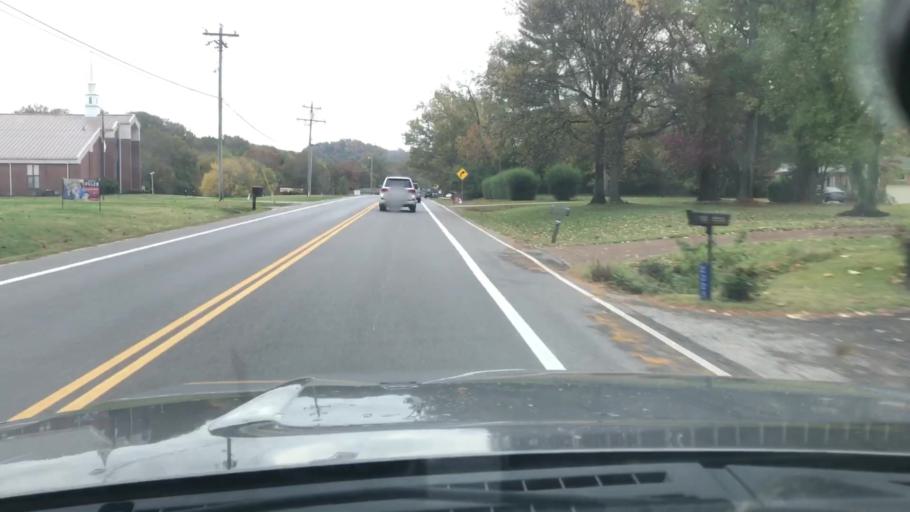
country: US
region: Tennessee
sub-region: Davidson County
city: Forest Hills
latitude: 36.0054
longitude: -86.8862
